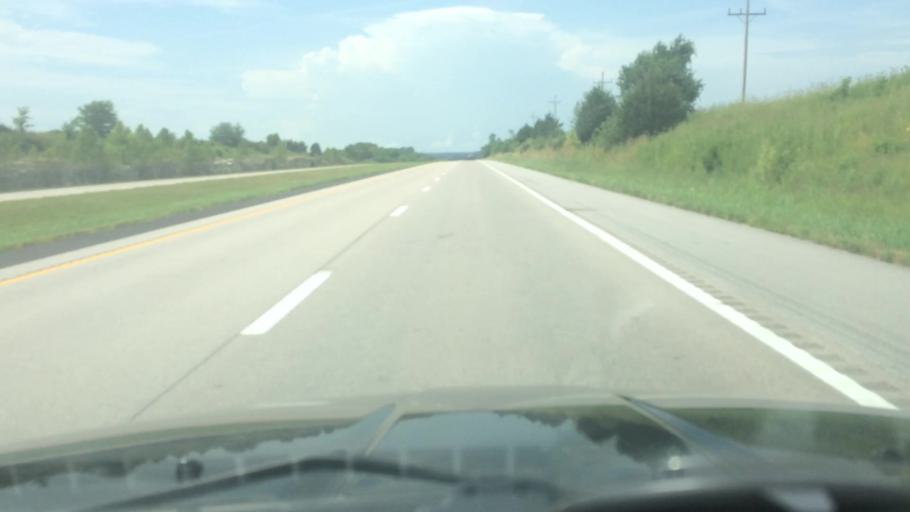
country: US
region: Missouri
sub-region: Polk County
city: Humansville
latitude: 37.8009
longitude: -93.5951
